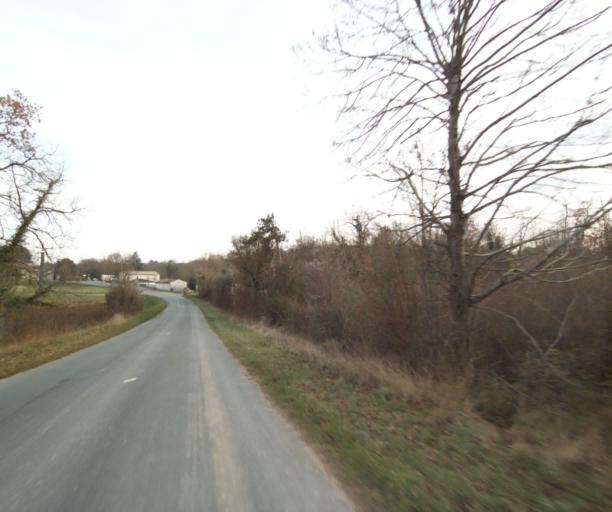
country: FR
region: Poitou-Charentes
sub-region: Departement de la Charente-Maritime
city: Fontcouverte
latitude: 45.7963
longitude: -0.5686
